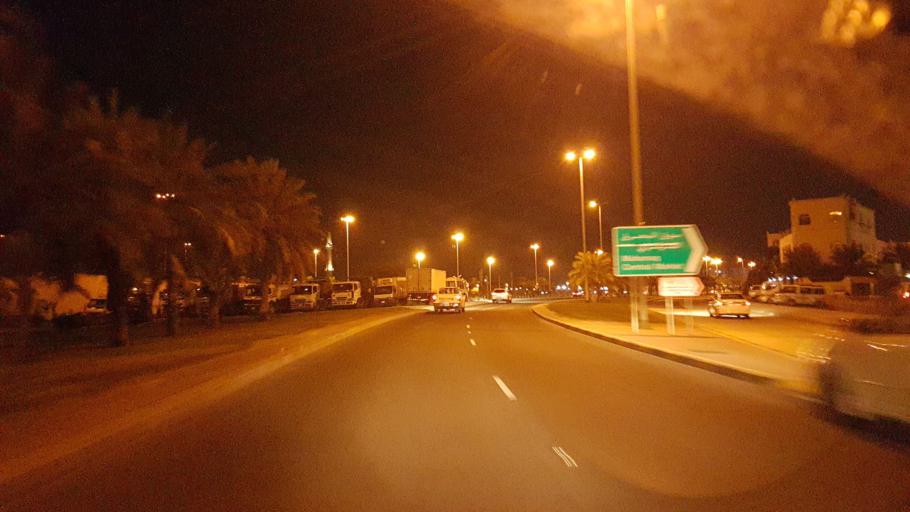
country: BH
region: Muharraq
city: Al Muharraq
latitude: 26.2521
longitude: 50.6055
